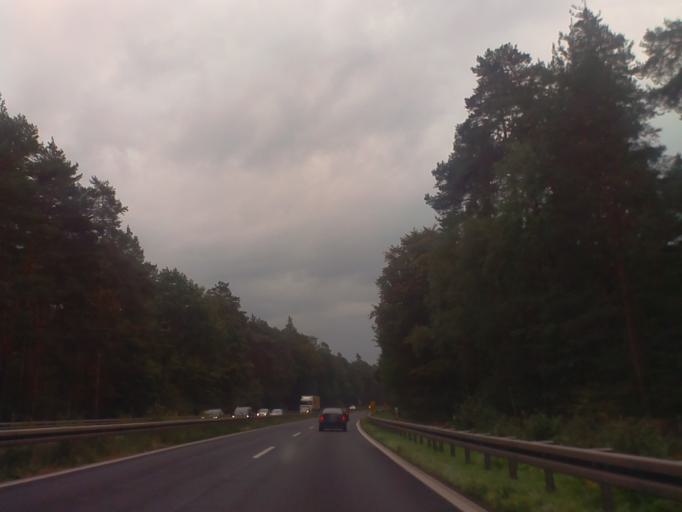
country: DE
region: Bavaria
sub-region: Regierungsbezirk Unterfranken
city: Stockstadt am Main
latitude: 49.9653
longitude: 9.0508
